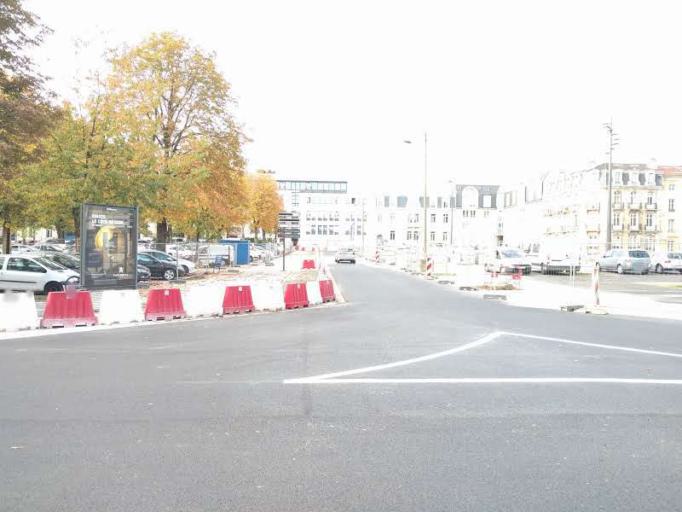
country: FR
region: Lorraine
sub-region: Departement de Meurthe-et-Moselle
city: Maxeville
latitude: 48.6978
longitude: 6.1752
